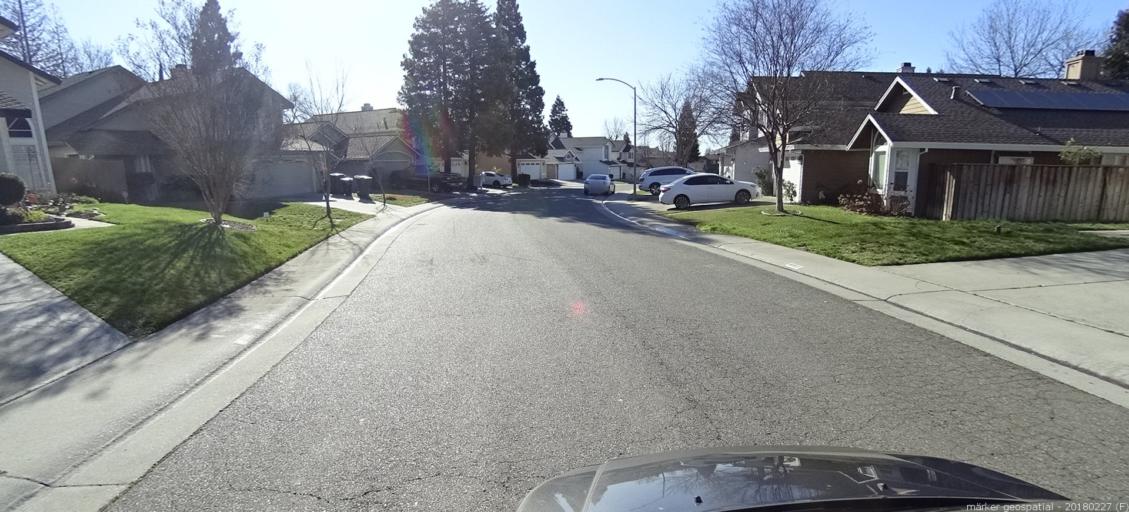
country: US
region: California
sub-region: Sacramento County
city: North Highlands
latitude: 38.7182
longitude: -121.3702
